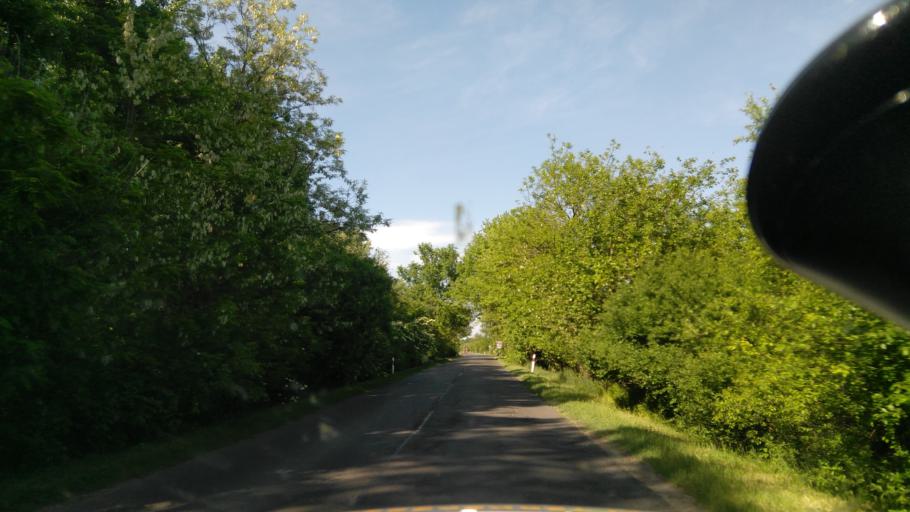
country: HU
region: Bekes
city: Gyula
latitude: 46.6783
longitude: 21.3027
